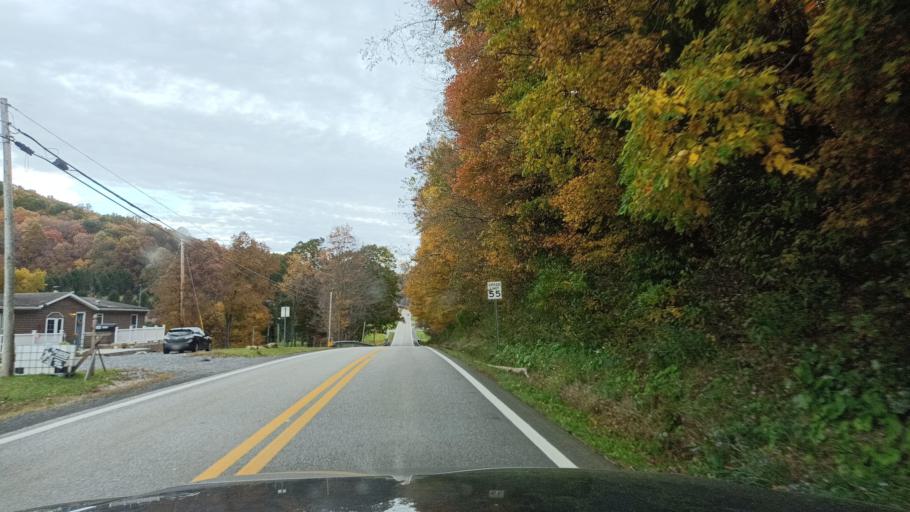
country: US
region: West Virginia
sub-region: Taylor County
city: Grafton
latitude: 39.3599
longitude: -79.9901
